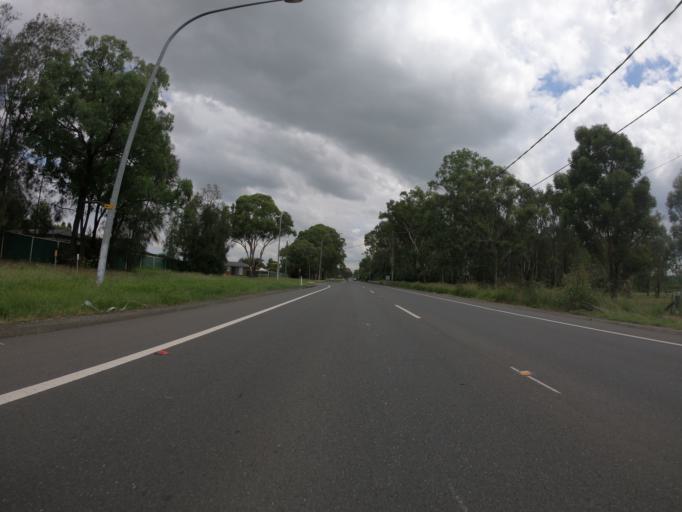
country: AU
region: New South Wales
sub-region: Blacktown
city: Mount Druitt
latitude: -33.7976
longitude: 150.7688
